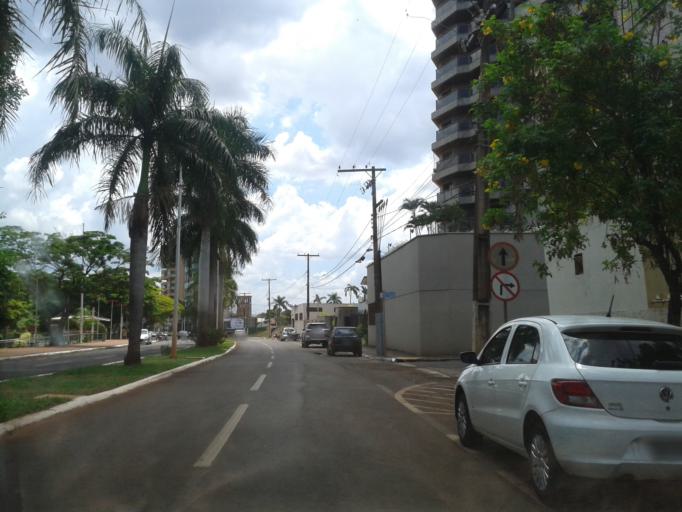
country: BR
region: Goias
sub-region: Itumbiara
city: Itumbiara
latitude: -18.4130
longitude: -49.2076
